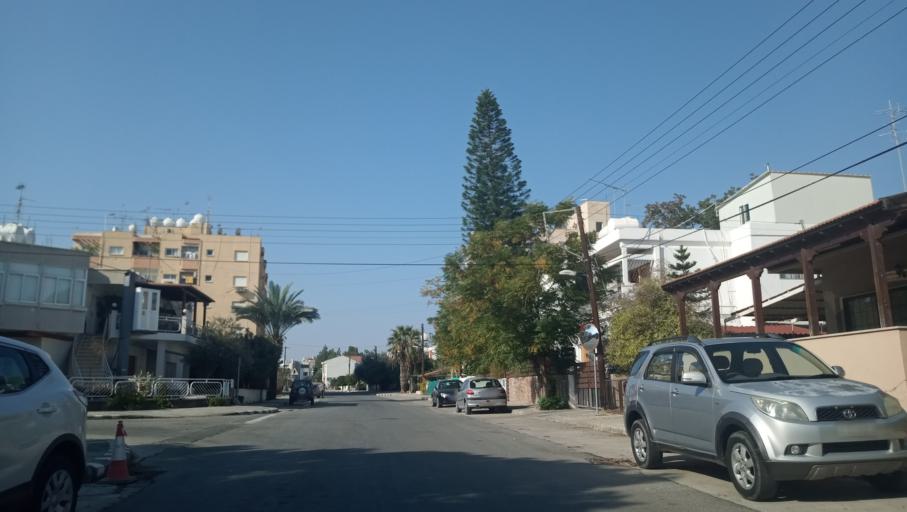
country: CY
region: Lefkosia
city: Nicosia
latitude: 35.1436
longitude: 33.3831
